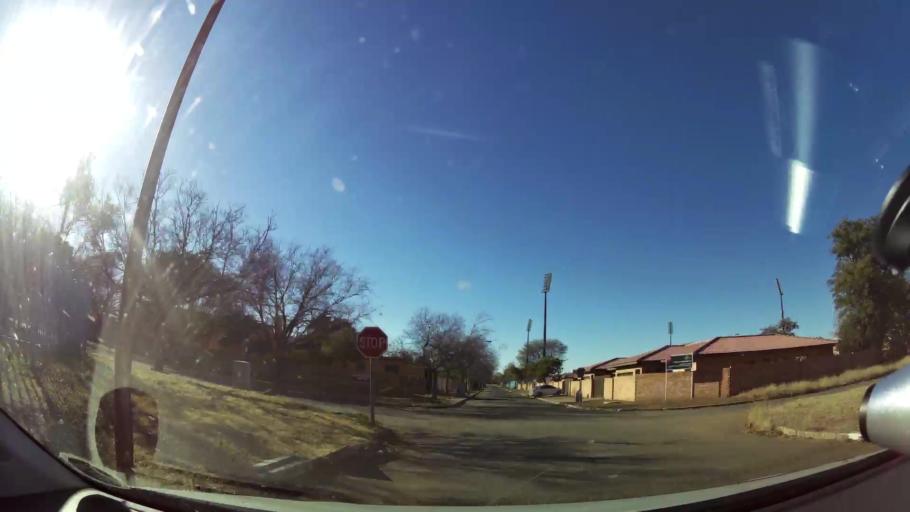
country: ZA
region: Northern Cape
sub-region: Frances Baard District Municipality
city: Kimberley
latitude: -28.7408
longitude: 24.7953
